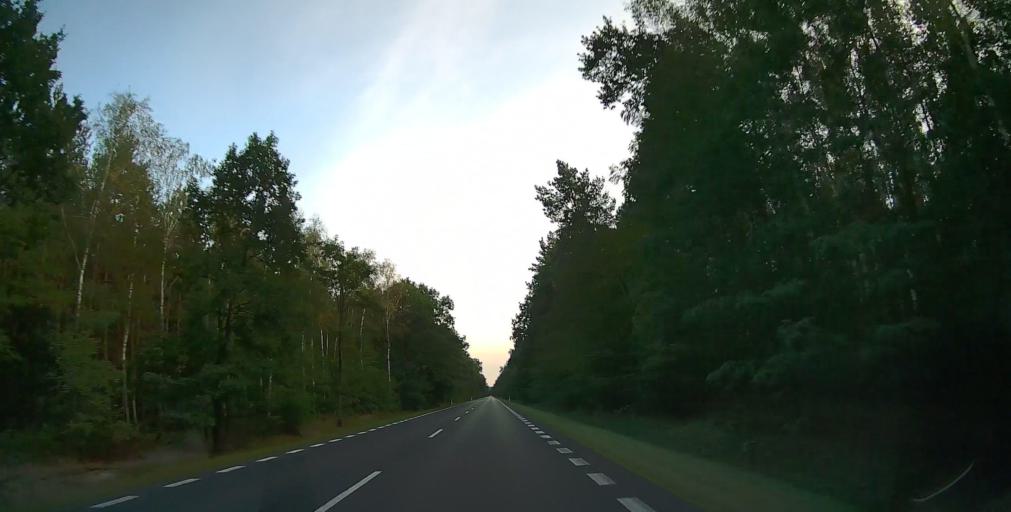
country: PL
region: Masovian Voivodeship
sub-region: Powiat kozienicki
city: Ryczywol
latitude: 51.7032
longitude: 21.4048
